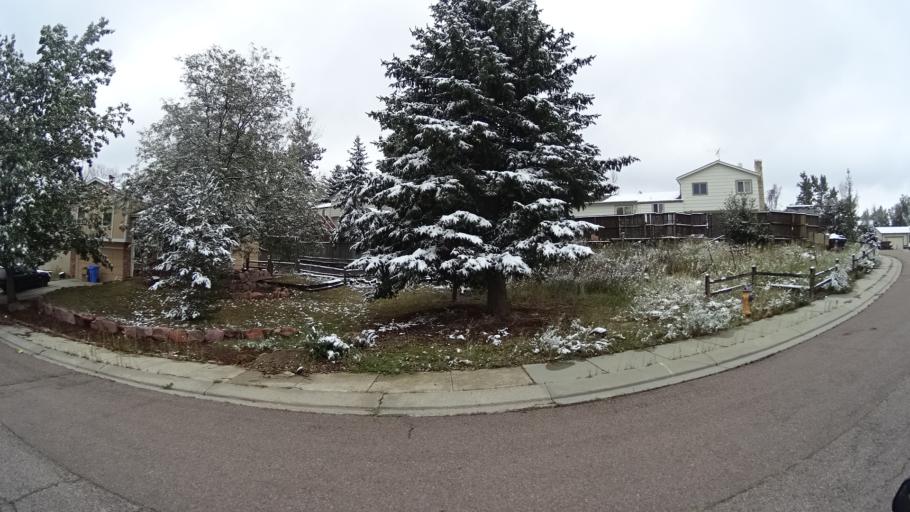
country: US
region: Colorado
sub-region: El Paso County
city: Colorado Springs
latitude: 38.9269
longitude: -104.7776
